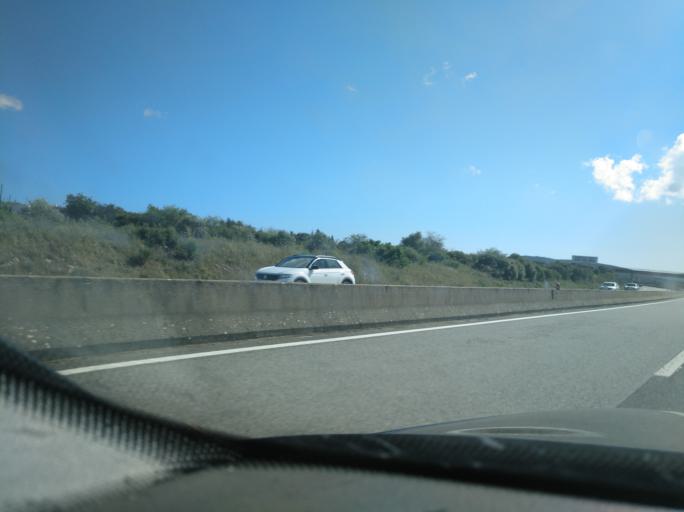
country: PT
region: Faro
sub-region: Olhao
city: Moncarapacho
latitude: 37.1334
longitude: -7.7543
